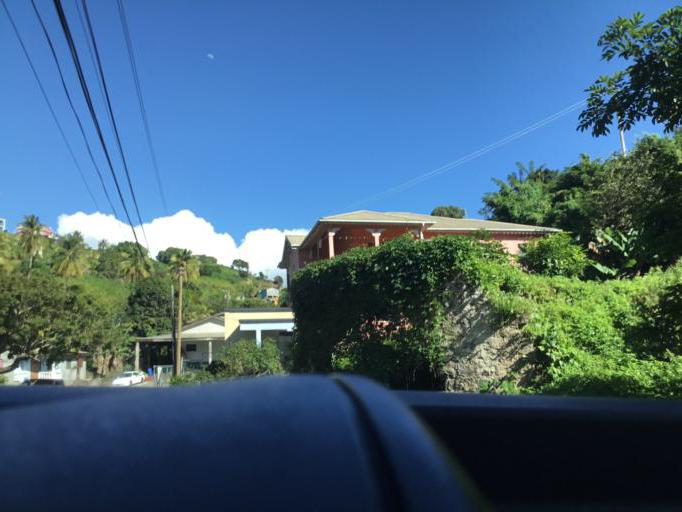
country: VC
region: Saint David
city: Chateaubelair
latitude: 13.2747
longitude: -61.2495
